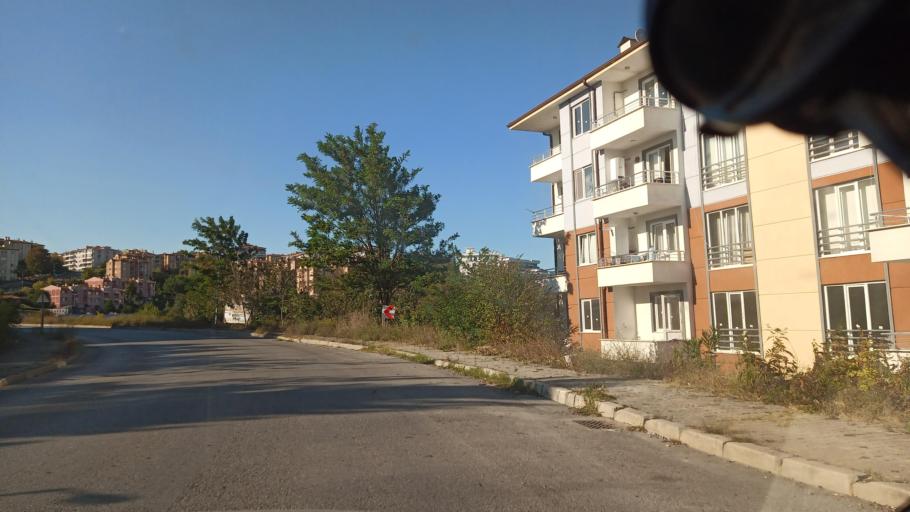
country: TR
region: Sakarya
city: Kazimpasa
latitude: 40.8566
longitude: 30.2945
